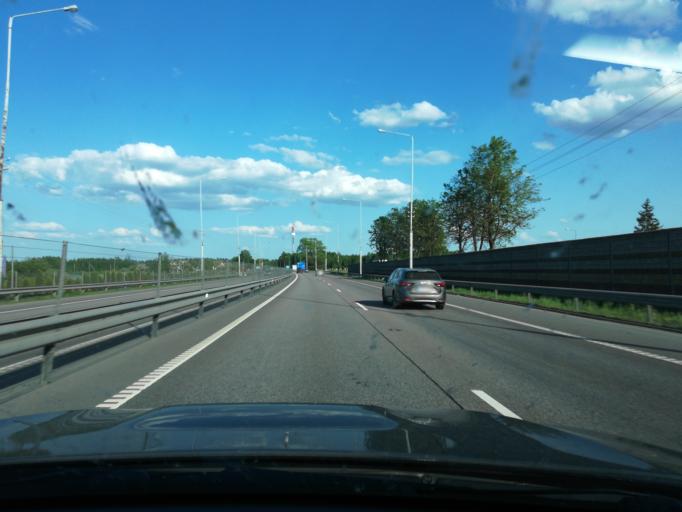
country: LT
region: Vilnius County
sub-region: Vilniaus Rajonas
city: Vievis
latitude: 54.7704
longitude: 24.8250
